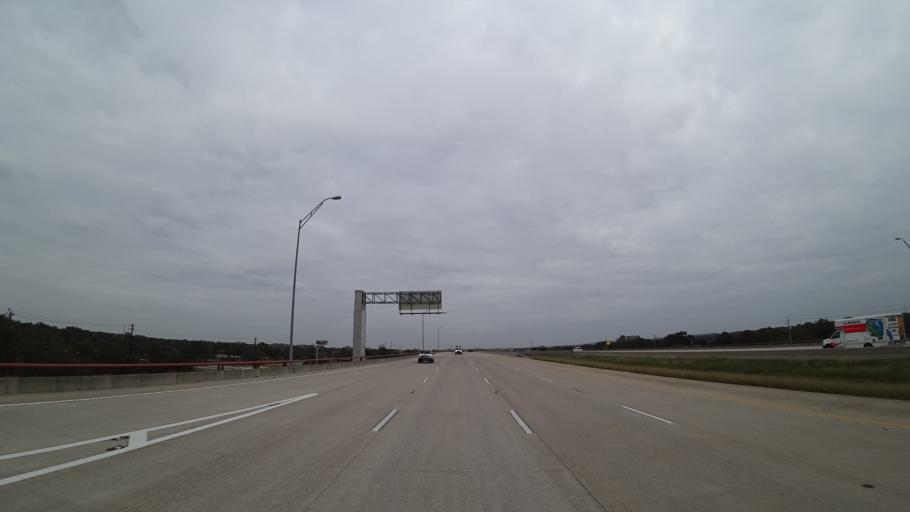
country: US
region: Texas
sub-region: Williamson County
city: Brushy Creek
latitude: 30.4814
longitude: -97.7462
